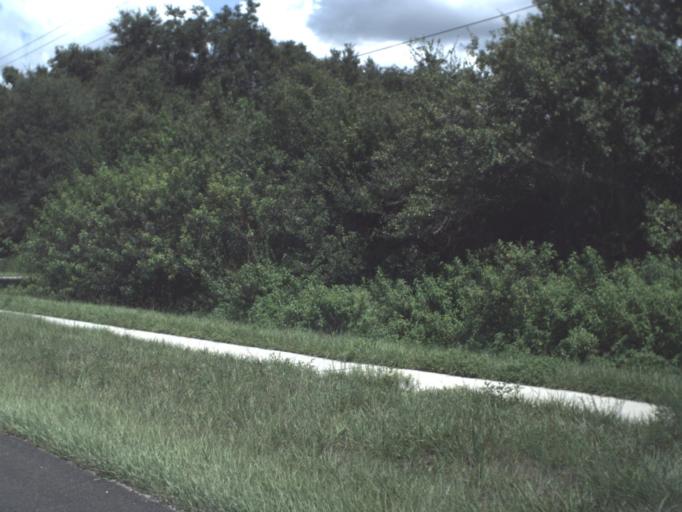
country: US
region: Florida
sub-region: Hillsborough County
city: Ruskin
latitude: 27.6903
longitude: -82.4665
